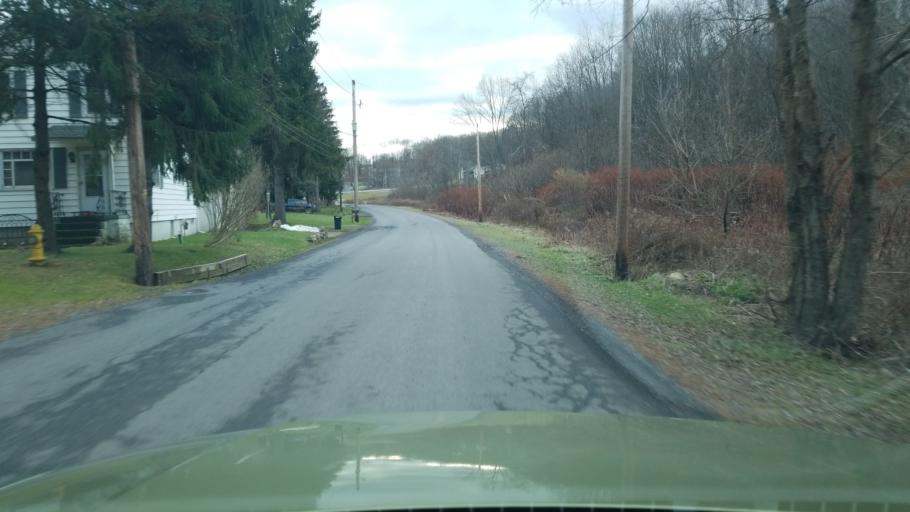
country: US
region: Pennsylvania
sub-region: Clearfield County
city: DuBois
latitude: 41.1264
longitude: -78.7772
